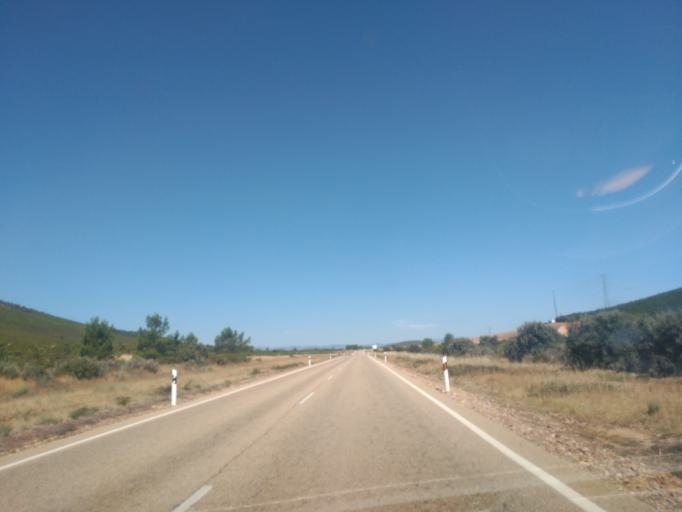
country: ES
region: Castille and Leon
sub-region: Provincia de Zamora
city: Tabara
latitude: 41.8727
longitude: -6.0094
